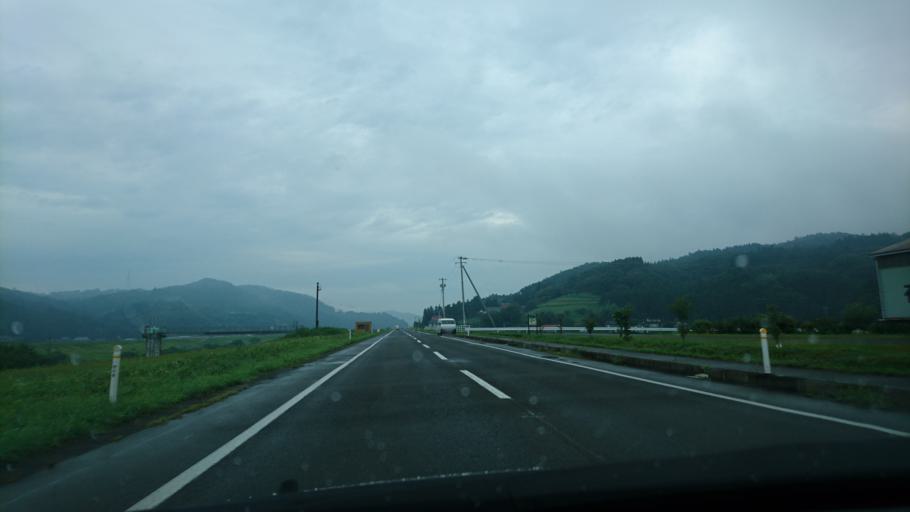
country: JP
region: Iwate
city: Ichinoseki
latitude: 38.9081
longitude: 141.2592
